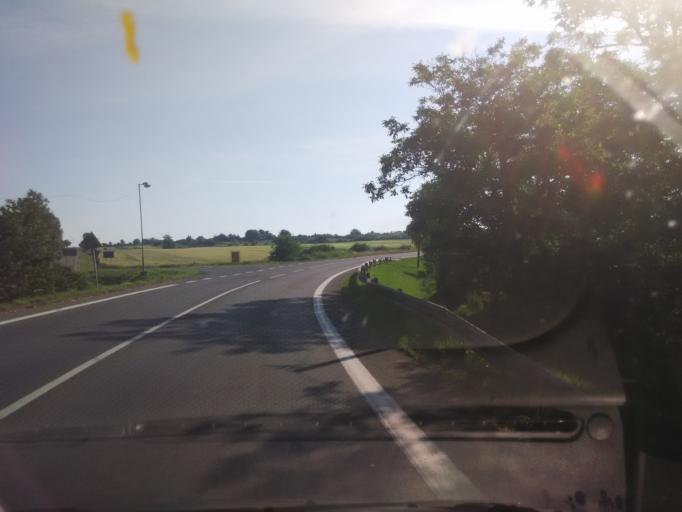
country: SK
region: Nitriansky
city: Levice
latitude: 48.2634
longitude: 18.7089
